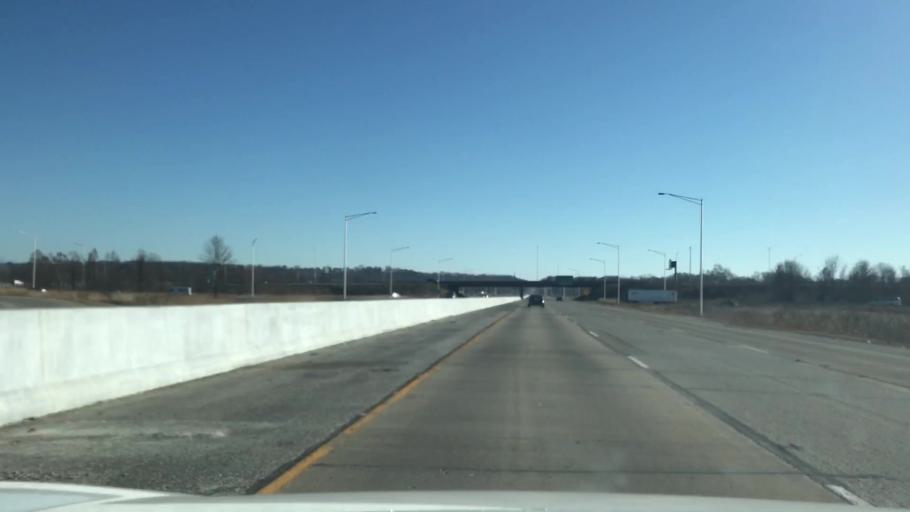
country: US
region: Illinois
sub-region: Saint Clair County
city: Alorton
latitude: 38.5850
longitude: -90.1106
